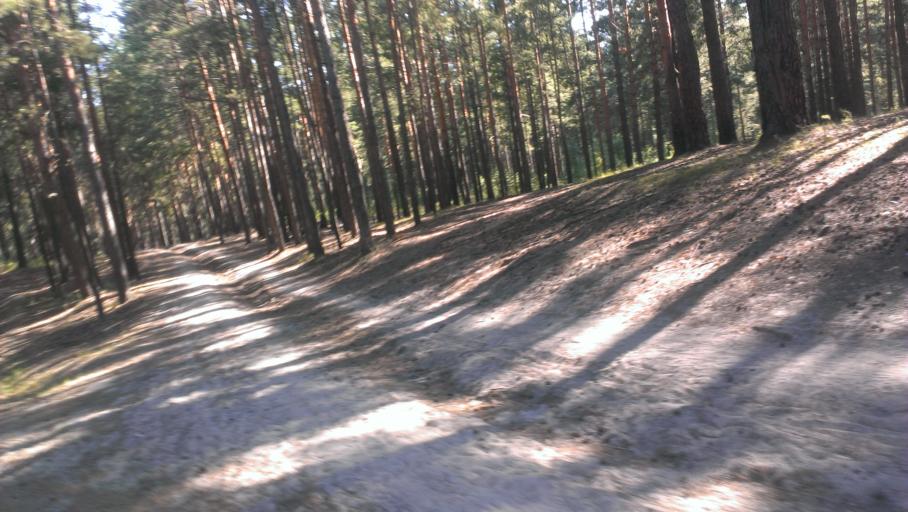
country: RU
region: Altai Krai
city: Novosilikatnyy
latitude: 53.3191
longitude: 83.6860
